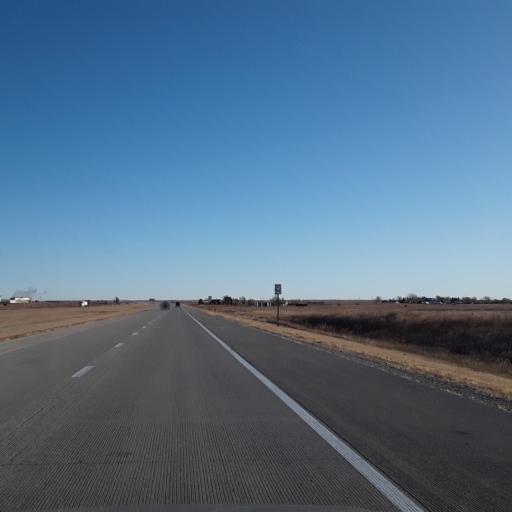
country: US
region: Kansas
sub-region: Seward County
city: Liberal
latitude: 37.0946
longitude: -100.8136
